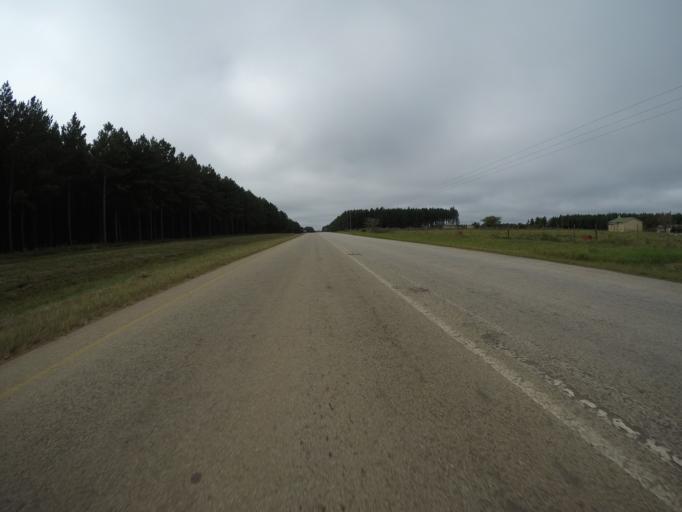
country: ZA
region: Eastern Cape
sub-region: Cacadu District Municipality
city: Kareedouw
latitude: -33.9952
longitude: 24.1262
